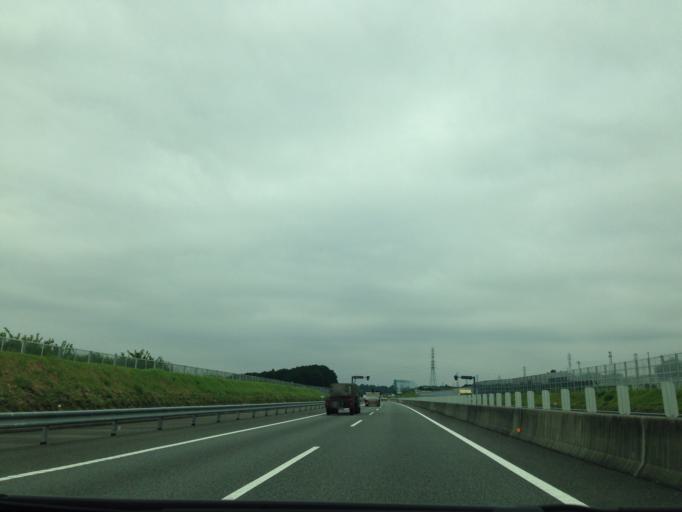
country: JP
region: Shizuoka
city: Fuji
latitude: 35.1903
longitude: 138.7158
